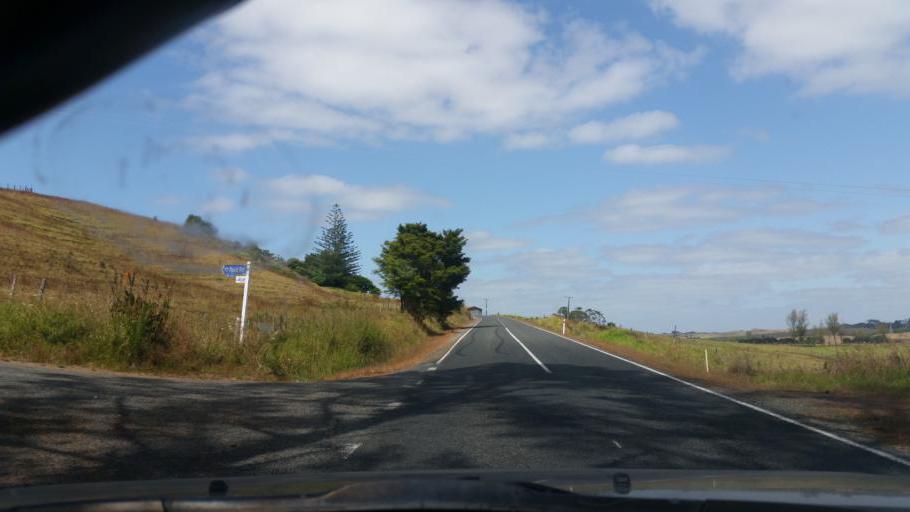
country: NZ
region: Northland
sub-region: Whangarei
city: Ruakaka
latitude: -35.9501
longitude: 174.2937
